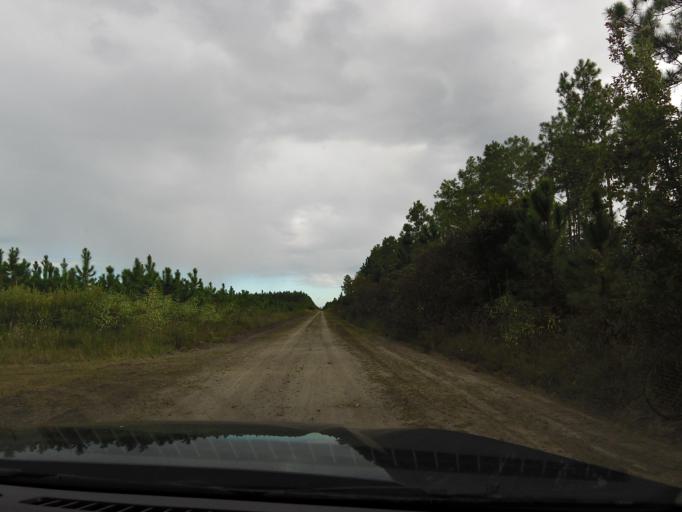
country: US
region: Florida
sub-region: Flagler County
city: Bunnell
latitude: 29.5610
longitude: -81.3332
